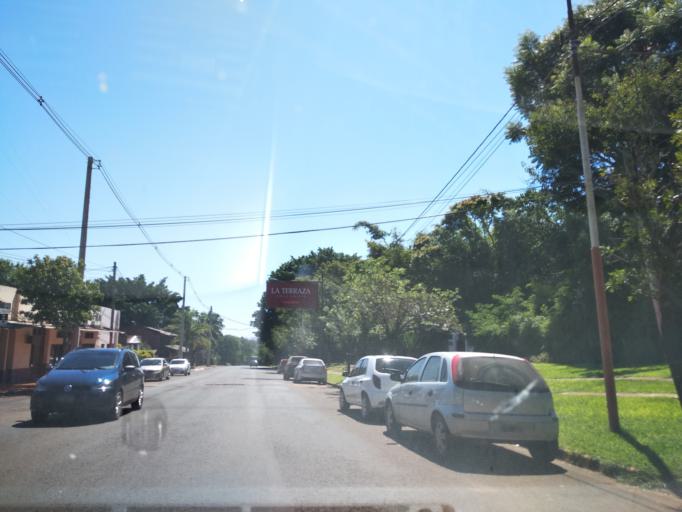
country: AR
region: Misiones
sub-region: Departamento de Iguazu
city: Puerto Iguazu
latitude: -25.6044
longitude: -54.5656
